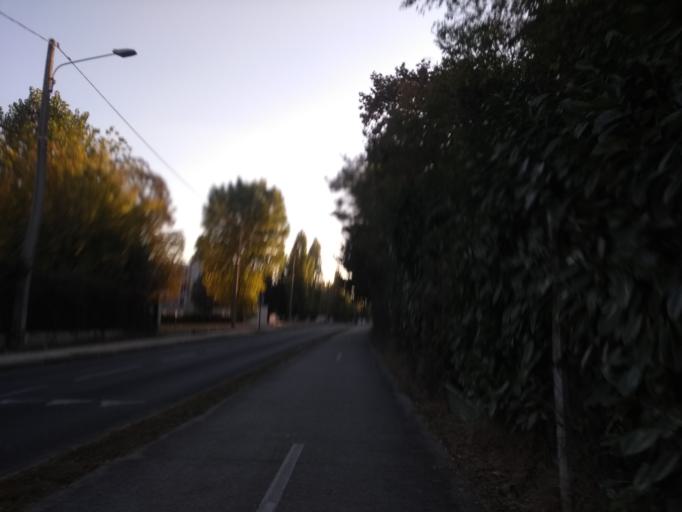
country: FR
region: Aquitaine
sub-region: Departement de la Gironde
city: Gradignan
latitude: 44.7839
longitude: -0.6122
